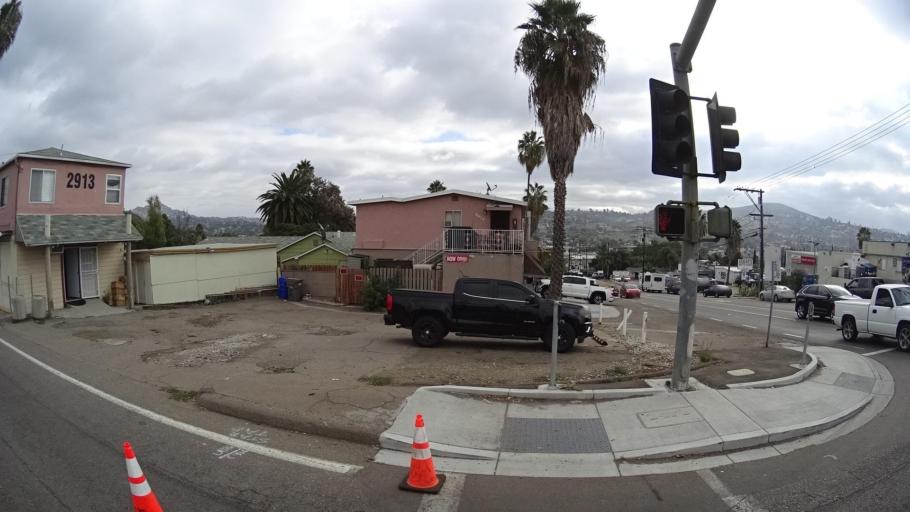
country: US
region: California
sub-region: San Diego County
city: Spring Valley
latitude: 32.7368
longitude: -117.0144
